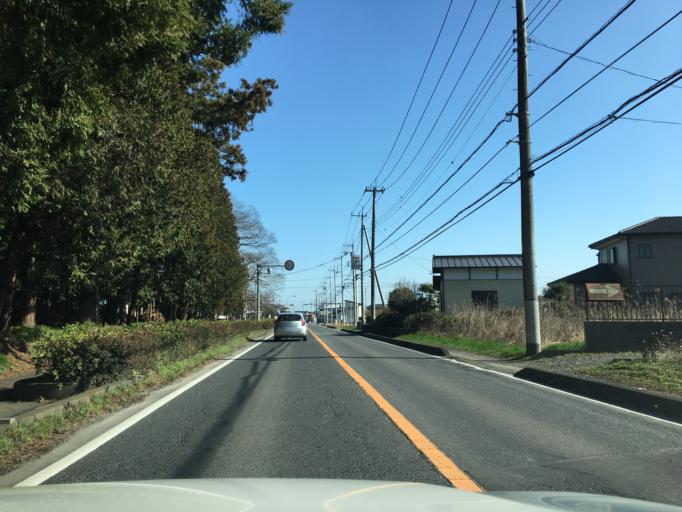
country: JP
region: Ibaraki
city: Omiya
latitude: 36.5189
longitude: 140.3629
